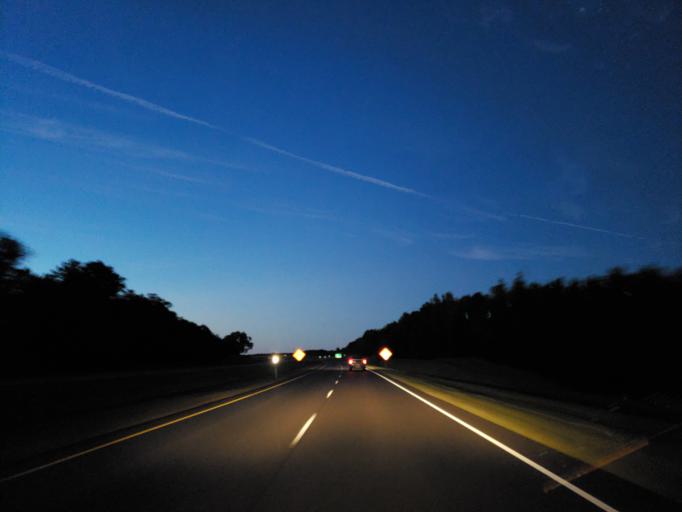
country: US
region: Mississippi
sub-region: Clarke County
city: Quitman
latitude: 32.0504
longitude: -88.6765
